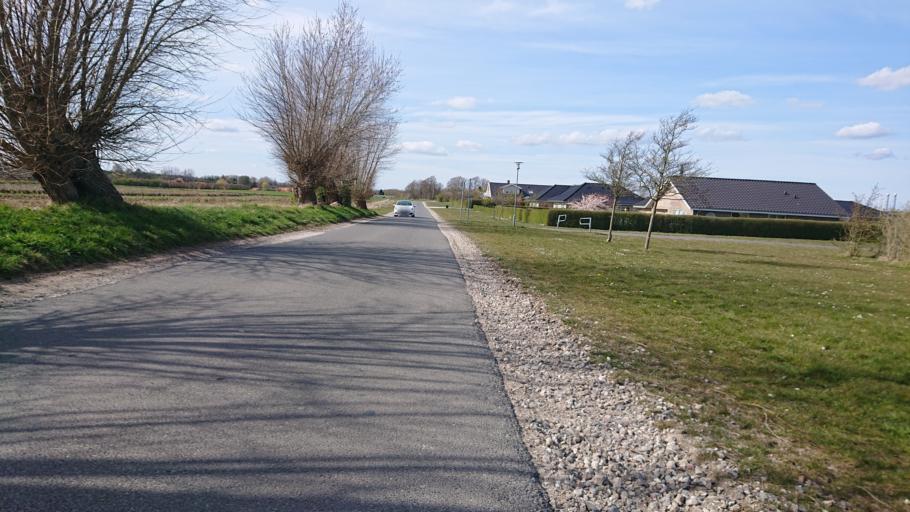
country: DK
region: South Denmark
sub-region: Nyborg Kommune
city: Nyborg
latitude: 55.3080
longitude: 10.7482
